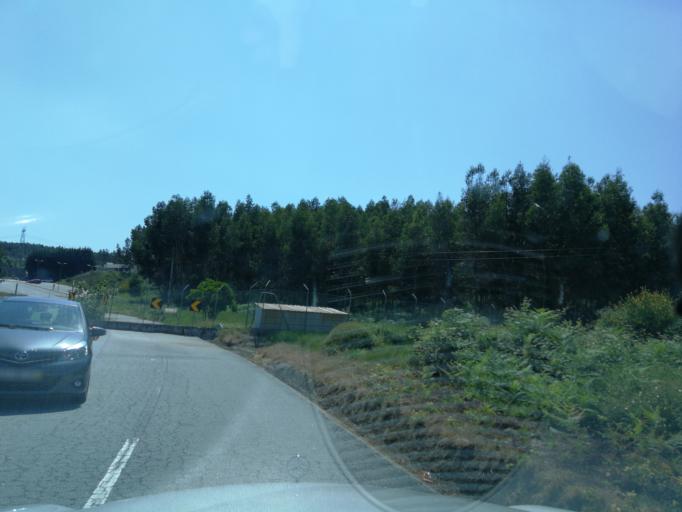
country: PT
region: Braga
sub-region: Povoa de Lanhoso
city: Povoa de Lanhoso
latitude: 41.5810
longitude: -8.3179
